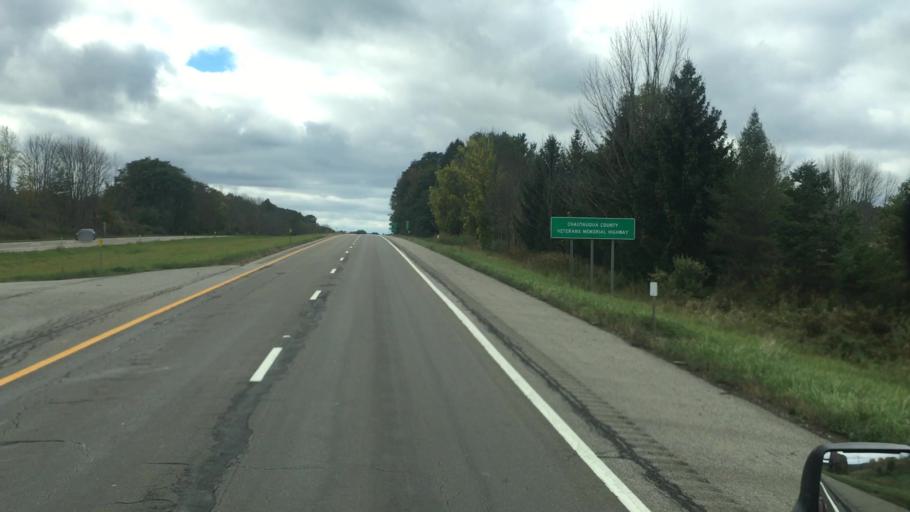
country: US
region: New York
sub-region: Cattaraugus County
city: Randolph
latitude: 42.1515
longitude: -79.0638
